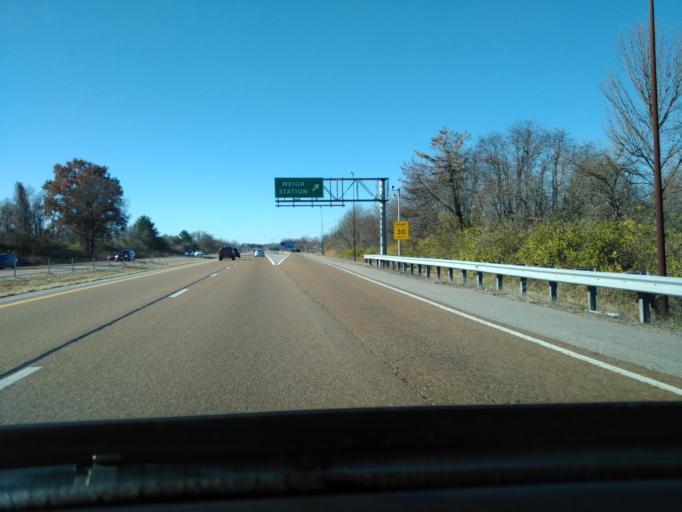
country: US
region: Illinois
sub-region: Madison County
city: Maryville
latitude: 38.7054
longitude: -89.9726
